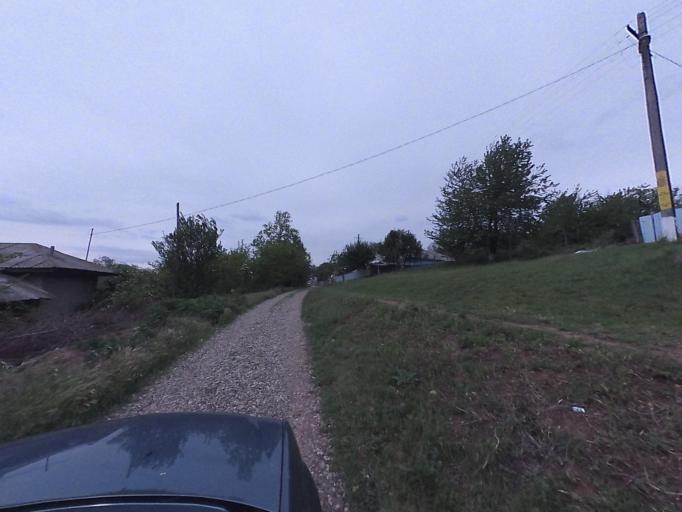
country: RO
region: Neamt
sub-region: Comuna Trifesti
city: Miron Costin
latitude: 46.9533
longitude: 26.8000
